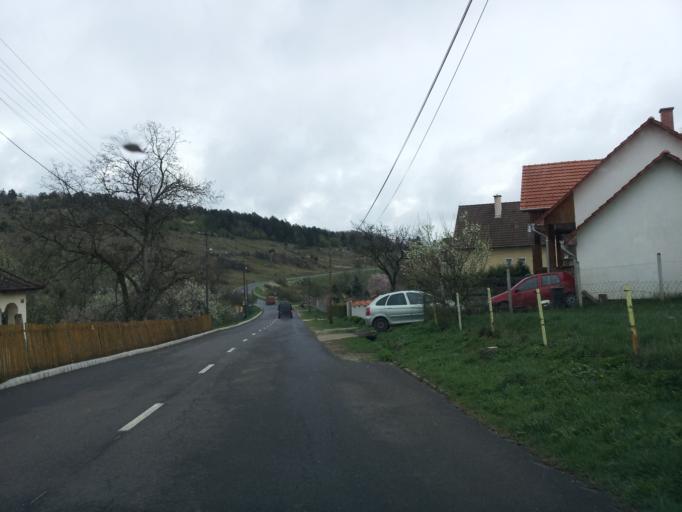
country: HU
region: Borsod-Abauj-Zemplen
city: Rudabanya
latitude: 48.4692
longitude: 20.5094
